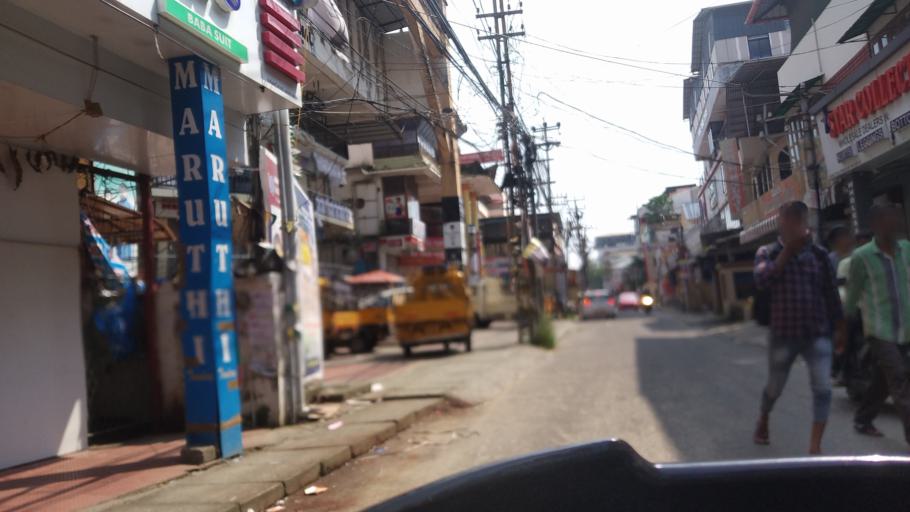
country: IN
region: Kerala
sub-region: Ernakulam
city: Cochin
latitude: 9.9780
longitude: 76.2797
